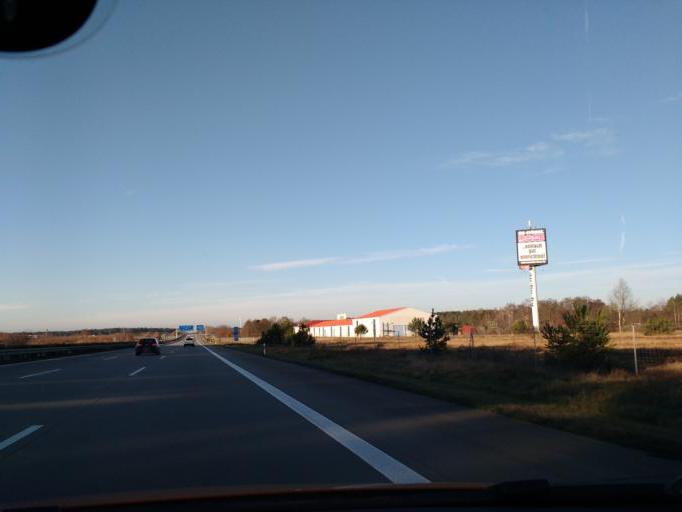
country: DE
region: Brandenburg
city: Ziesar
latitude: 52.2482
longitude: 12.2691
